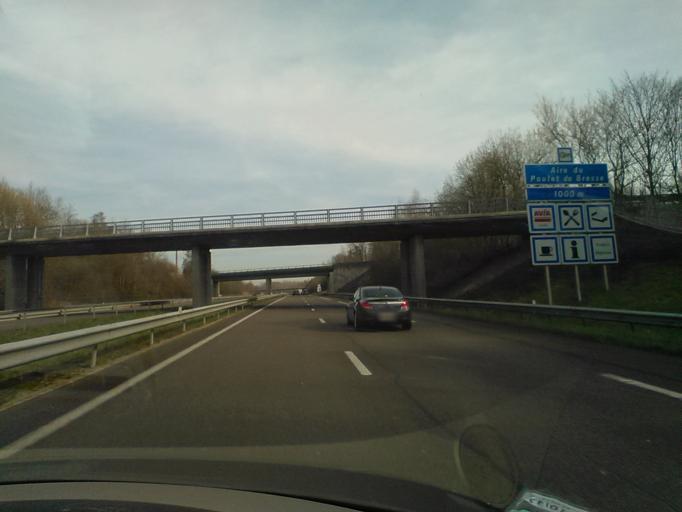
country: FR
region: Franche-Comte
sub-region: Departement du Jura
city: Saint-Amour
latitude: 46.4831
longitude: 5.3057
